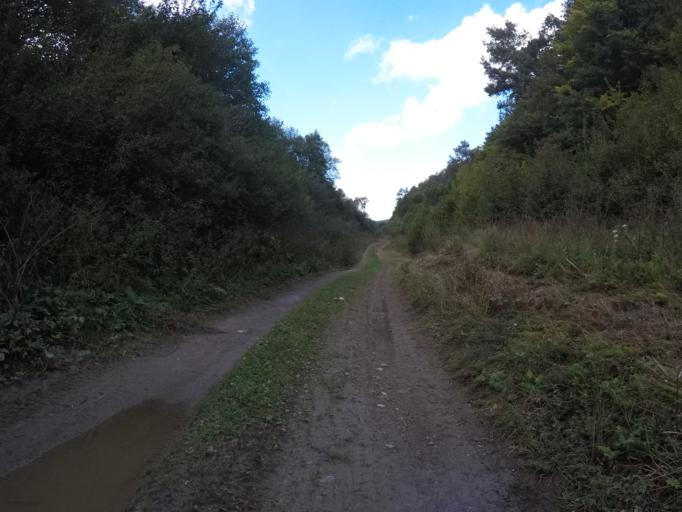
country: SK
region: Presovsky
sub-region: Okres Presov
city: Presov
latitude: 48.9299
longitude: 21.1705
